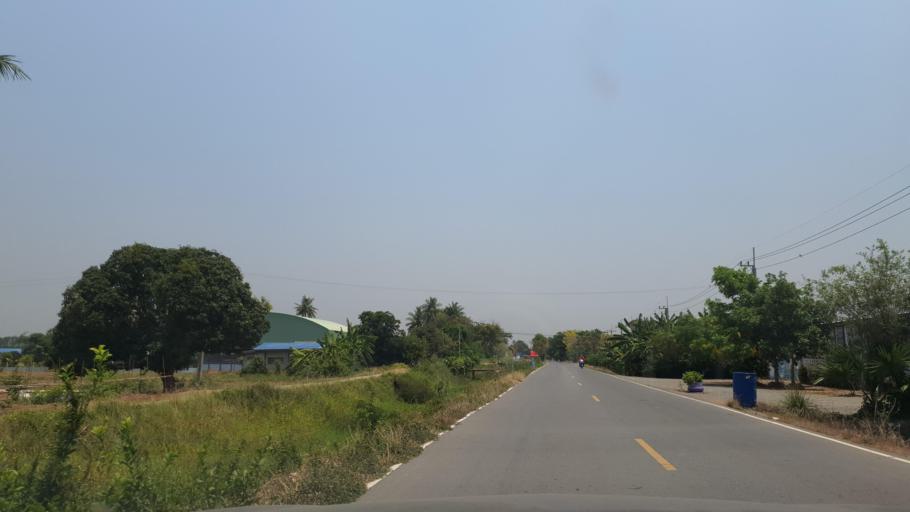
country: TH
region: Suphan Buri
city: Si Prachan
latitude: 14.5788
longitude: 100.1074
